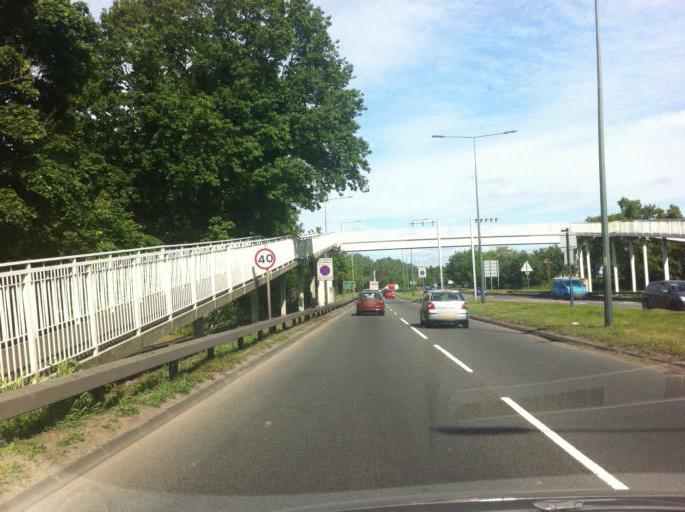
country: GB
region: England
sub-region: Greater London
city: Feltham
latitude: 51.4815
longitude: -0.4042
